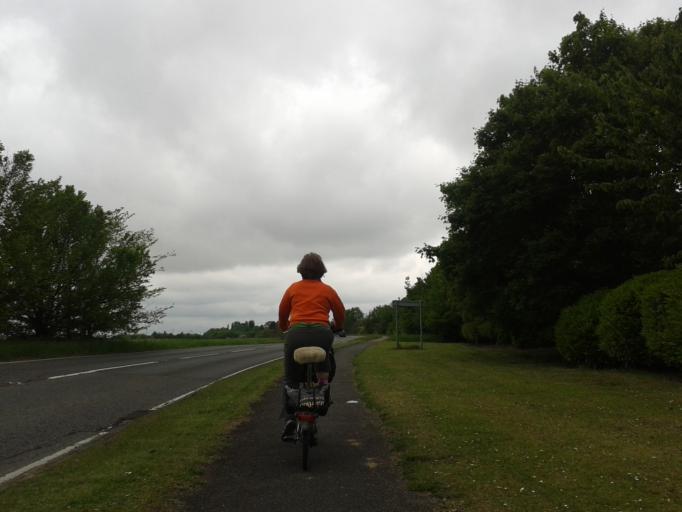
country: GB
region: England
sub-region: Cambridgeshire
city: Great Stukeley
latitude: 52.3459
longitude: -0.1996
